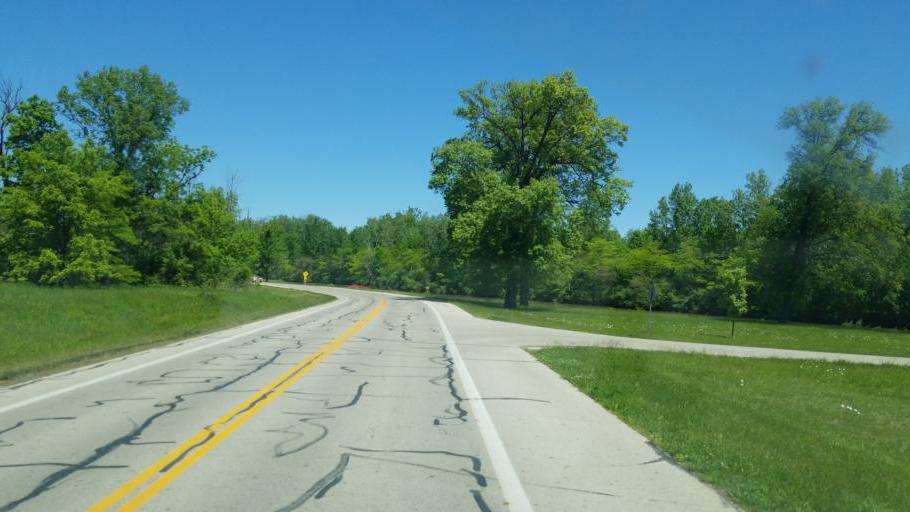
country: US
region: Ohio
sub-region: Auglaize County
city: Minster
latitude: 40.3828
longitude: -84.3599
